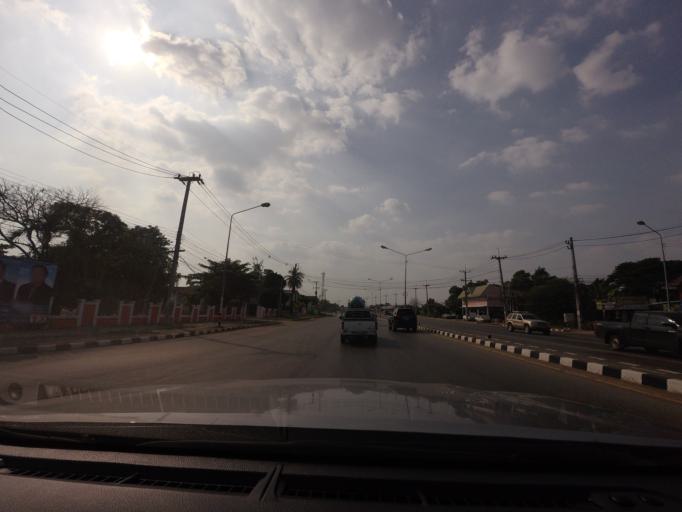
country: TH
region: Sukhothai
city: Sukhothai
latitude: 17.0261
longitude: 99.8817
